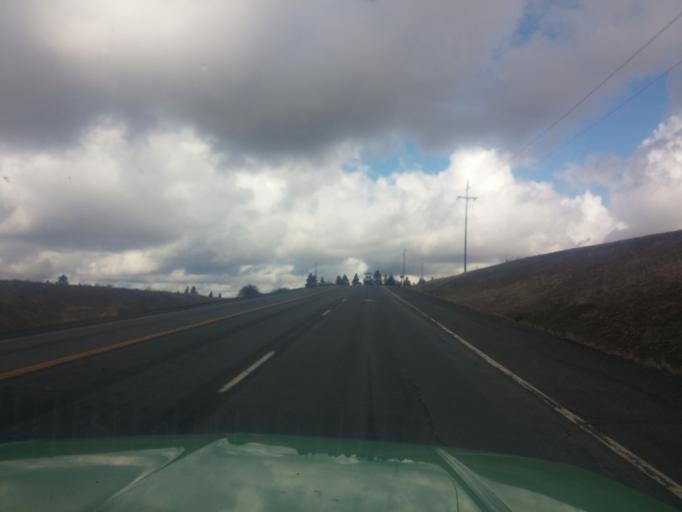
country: US
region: Idaho
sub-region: Latah County
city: Moscow
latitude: 46.8679
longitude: -117.0095
